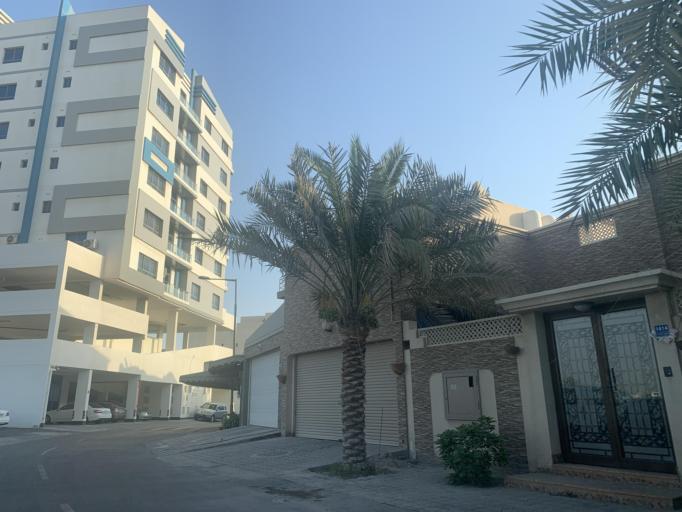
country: BH
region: Manama
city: Jidd Hafs
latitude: 26.1995
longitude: 50.5324
